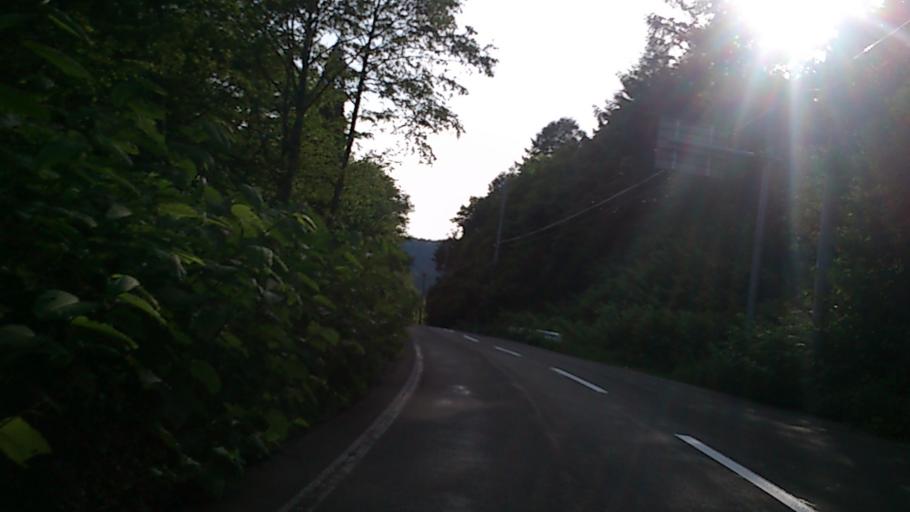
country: JP
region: Aomori
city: Aomori Shi
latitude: 40.6498
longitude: 140.7634
